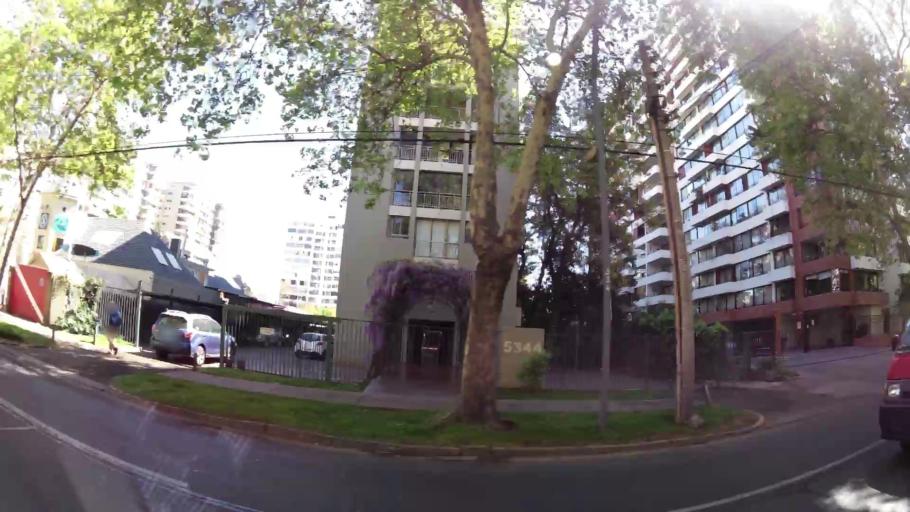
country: CL
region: Santiago Metropolitan
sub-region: Provincia de Santiago
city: Villa Presidente Frei, Nunoa, Santiago, Chile
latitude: -33.4183
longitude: -70.5703
